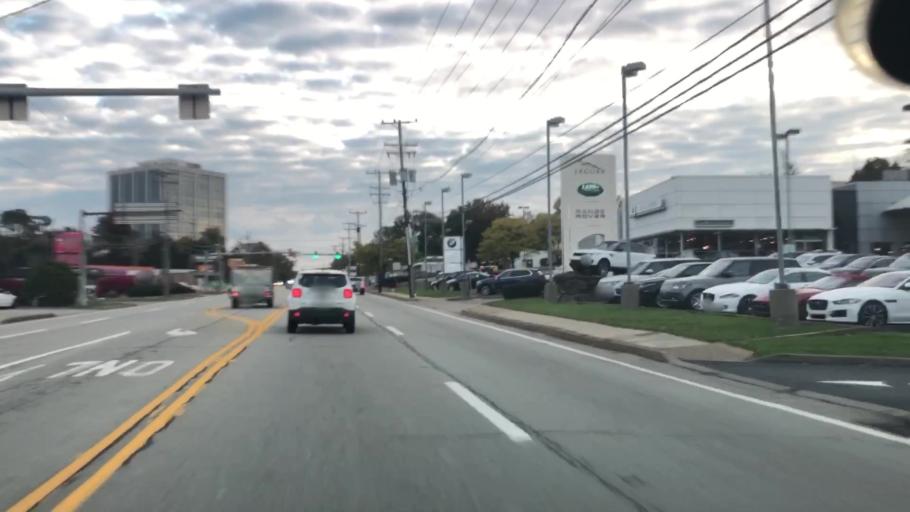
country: US
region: Pennsylvania
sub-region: Allegheny County
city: Monroeville
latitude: 40.4360
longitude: -79.7851
